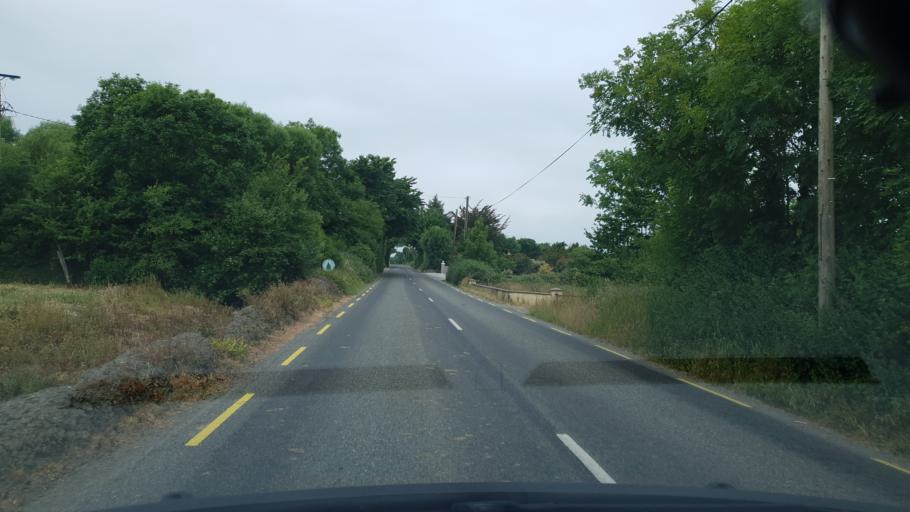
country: IE
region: Munster
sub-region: Ciarrai
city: Tralee
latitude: 52.1605
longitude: -9.6592
